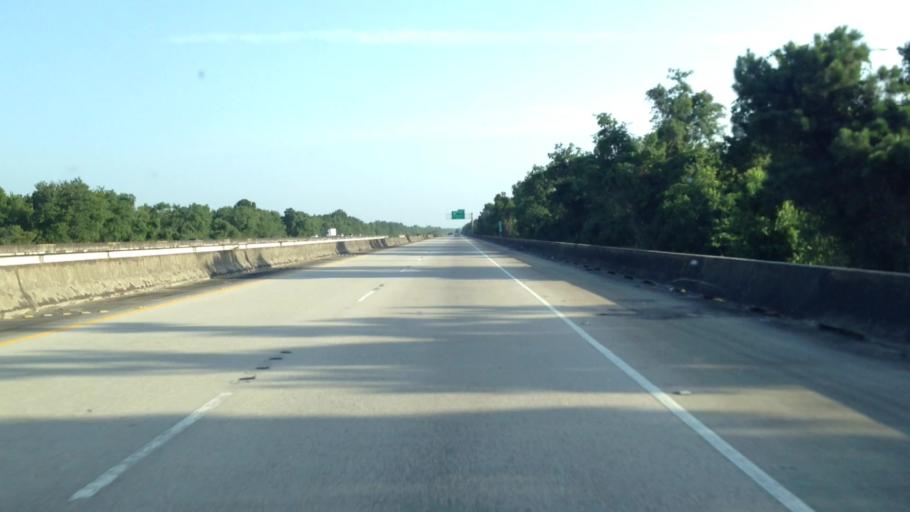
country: US
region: Louisiana
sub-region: Tangipahoa Parish
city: Ponchatoula
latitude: 30.3797
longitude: -90.4248
